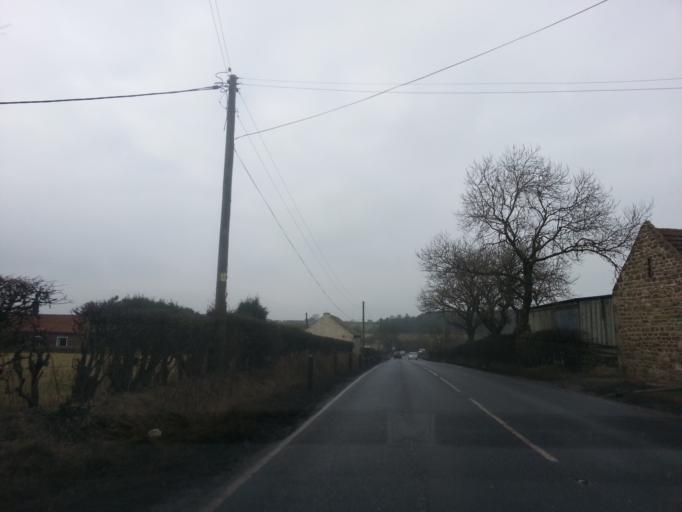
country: GB
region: England
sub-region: Darlington
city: Denton
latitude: 54.5971
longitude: -1.6620
